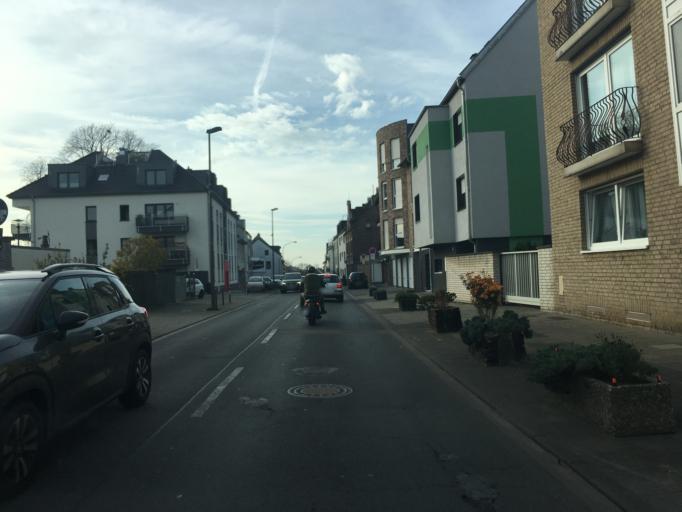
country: DE
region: North Rhine-Westphalia
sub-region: Regierungsbezirk Koln
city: Rath
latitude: 50.9467
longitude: 7.0838
